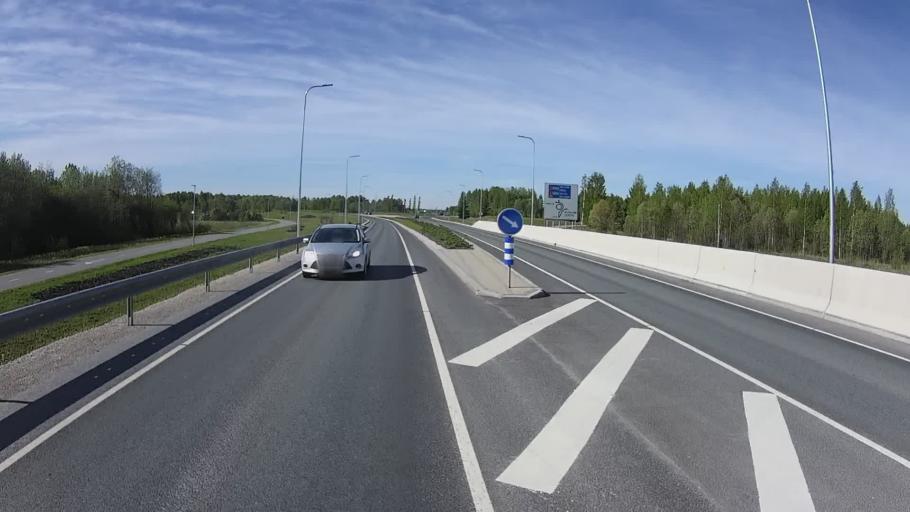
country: EE
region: Tartu
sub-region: Tartu linn
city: Tartu
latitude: 58.3647
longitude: 26.7749
